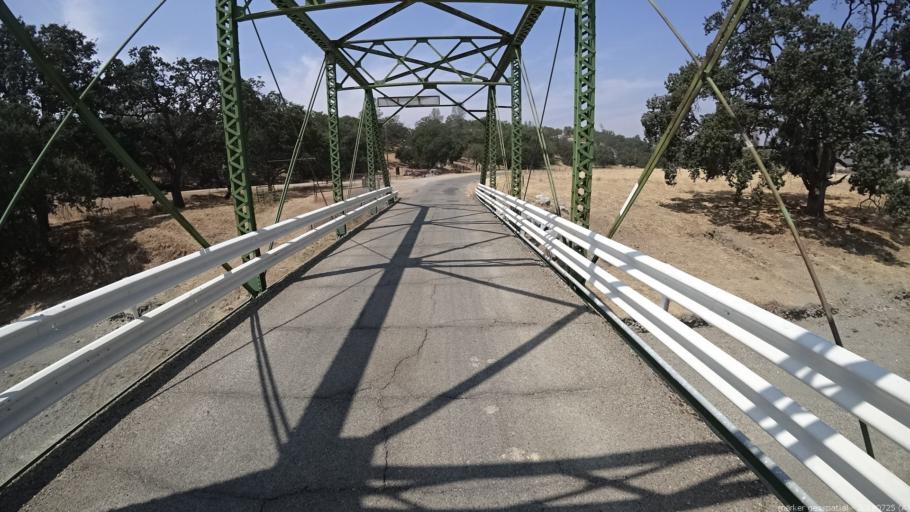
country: US
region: California
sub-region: Fresno County
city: Coalinga
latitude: 35.9099
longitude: -120.4373
